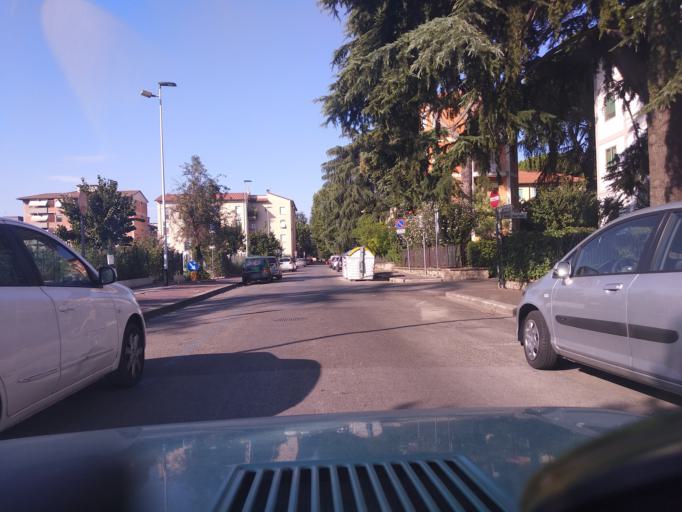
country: IT
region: Tuscany
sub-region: Province of Florence
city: Florence
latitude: 43.7785
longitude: 11.2130
